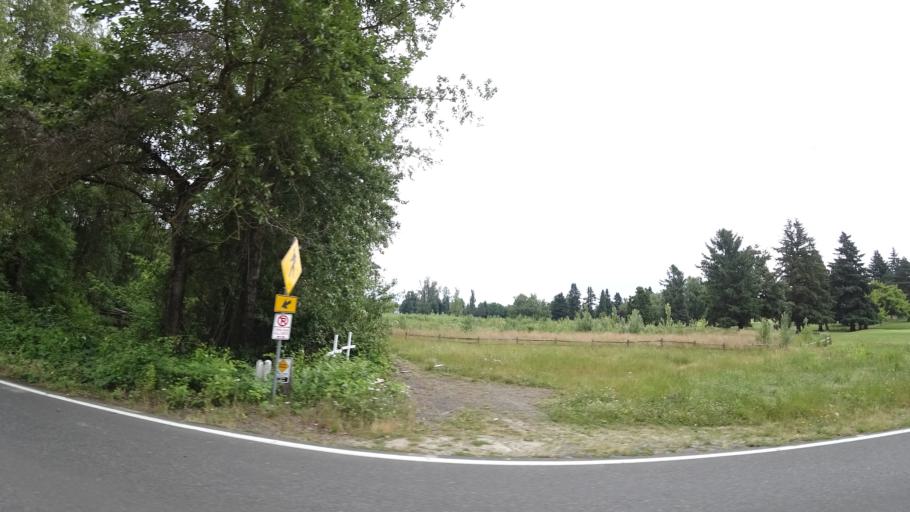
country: US
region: Oregon
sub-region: Multnomah County
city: Lents
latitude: 45.5707
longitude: -122.5871
